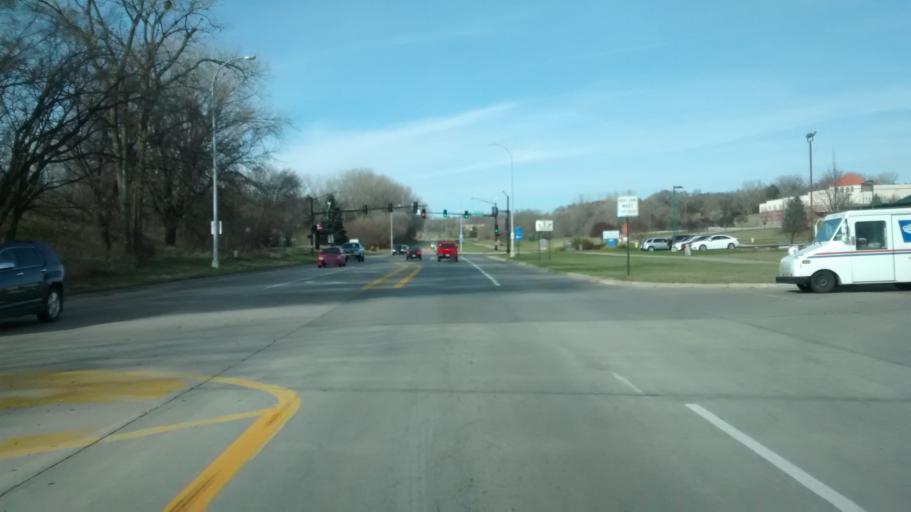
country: US
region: Iowa
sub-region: Woodbury County
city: Sioux City
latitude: 42.5360
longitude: -96.3732
